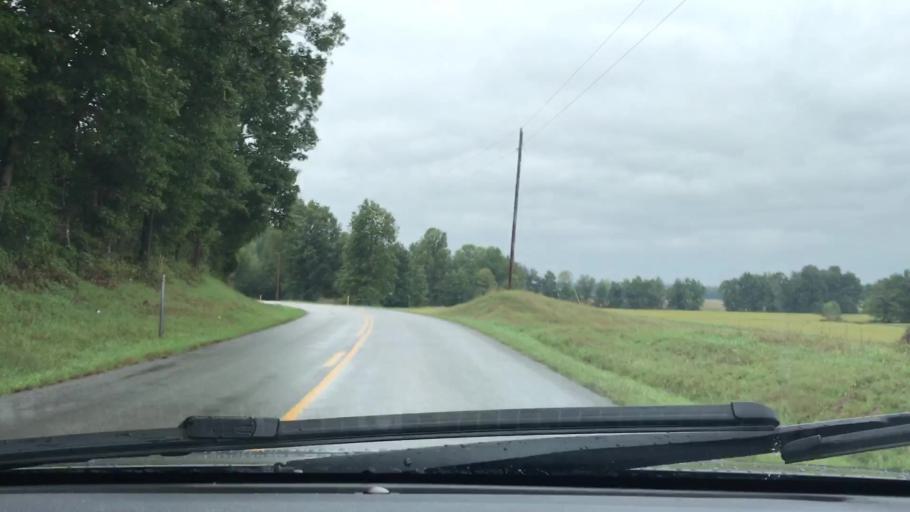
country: US
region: Kentucky
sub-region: McLean County
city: Calhoun
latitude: 37.4769
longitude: -87.2453
